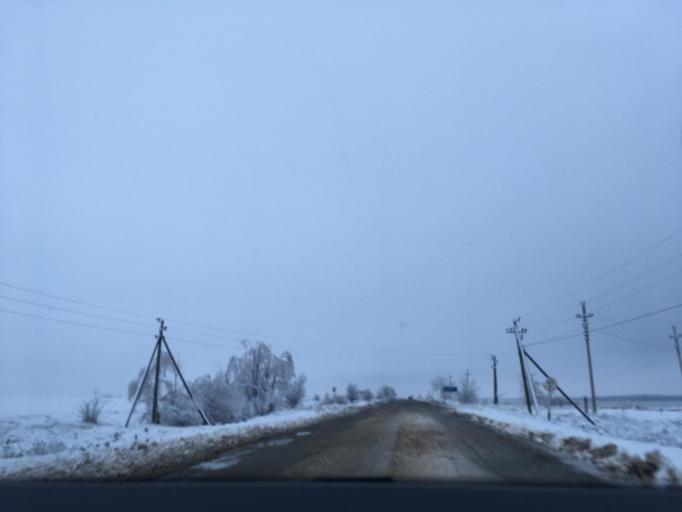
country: RU
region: Voronezj
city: Verkhniy Mamon
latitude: 50.0281
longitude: 40.0712
